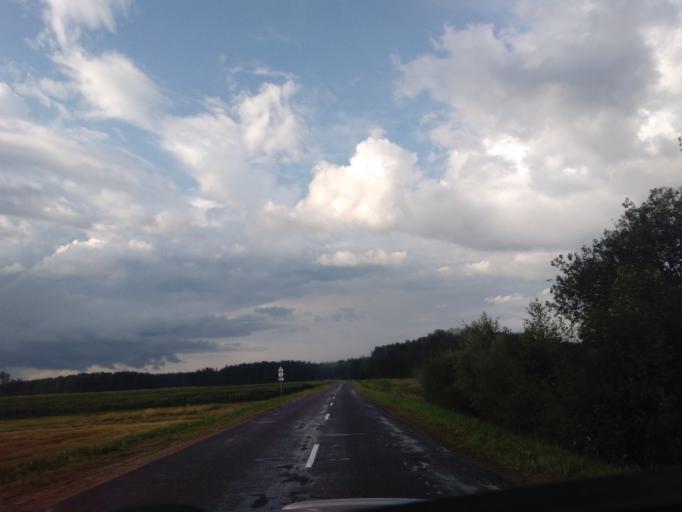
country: BY
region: Minsk
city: Uzda
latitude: 53.3501
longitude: 27.0948
